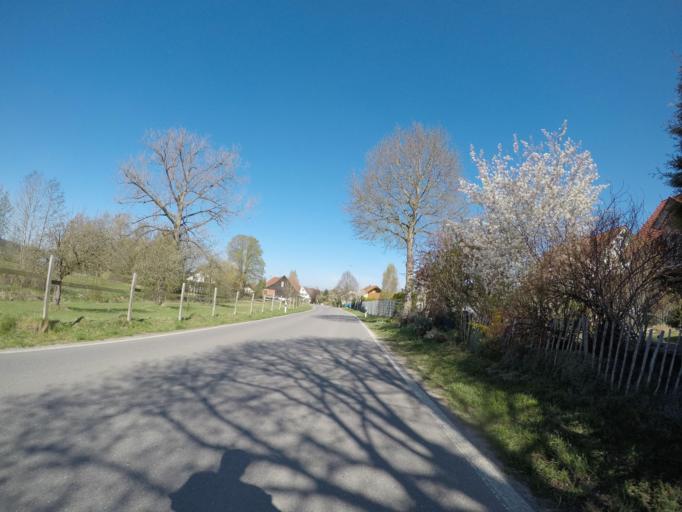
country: DE
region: Baden-Wuerttemberg
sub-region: Tuebingen Region
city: Fleischwangen
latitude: 47.8767
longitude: 9.4848
